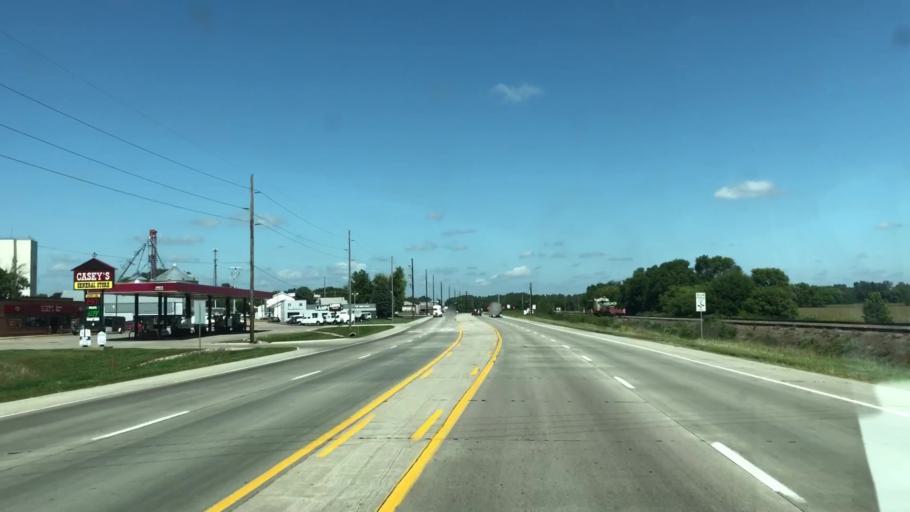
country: US
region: Iowa
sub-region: Plymouth County
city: Le Mars
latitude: 42.7162
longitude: -96.2483
